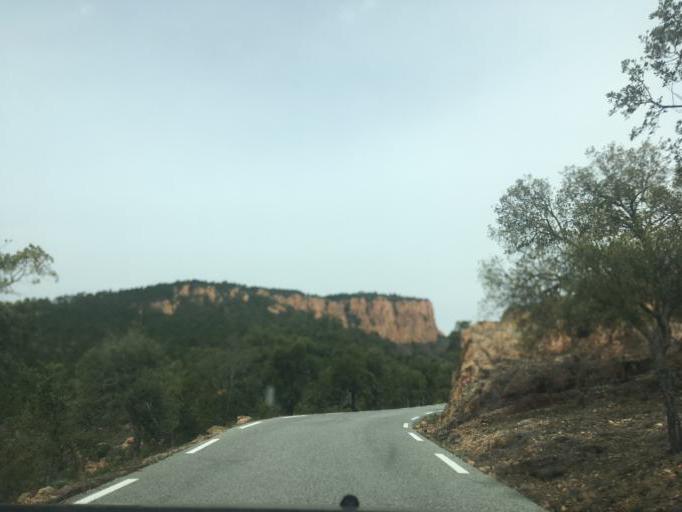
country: FR
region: Provence-Alpes-Cote d'Azur
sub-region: Departement du Var
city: Bagnols-en-Foret
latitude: 43.5180
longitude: 6.6511
